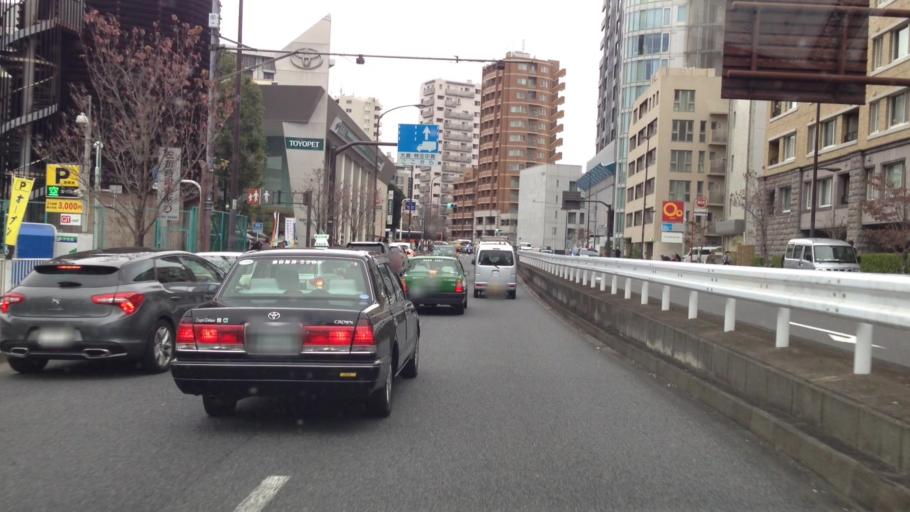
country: JP
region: Tokyo
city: Tokyo
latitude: 35.6403
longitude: 139.7323
